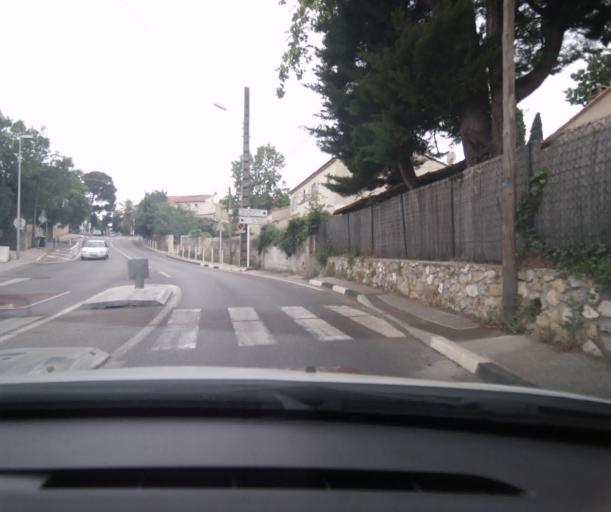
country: FR
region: Provence-Alpes-Cote d'Azur
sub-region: Departement du Var
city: La Valette-du-Var
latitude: 43.1105
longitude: 5.9801
